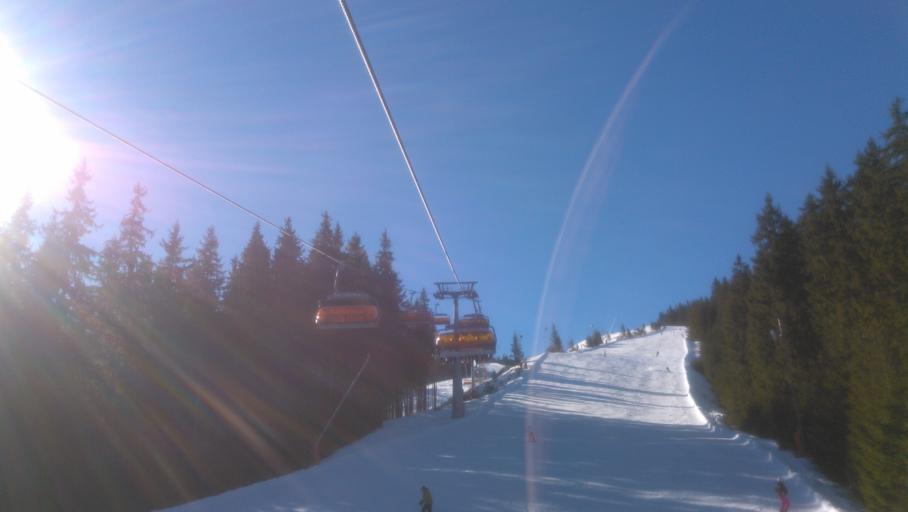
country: SK
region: Zilinsky
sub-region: Okres Liptovsky Mikulas
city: Liptovsky Mikulas
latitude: 48.9684
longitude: 19.5947
